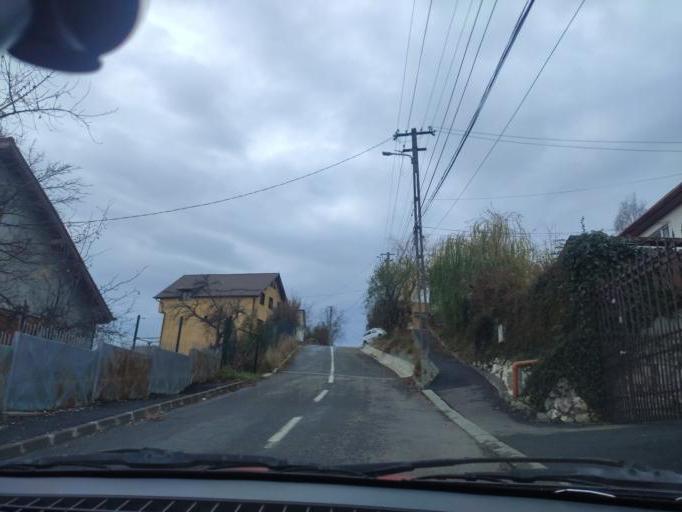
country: RO
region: Brasov
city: Codlea
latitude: 45.6995
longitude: 25.4364
